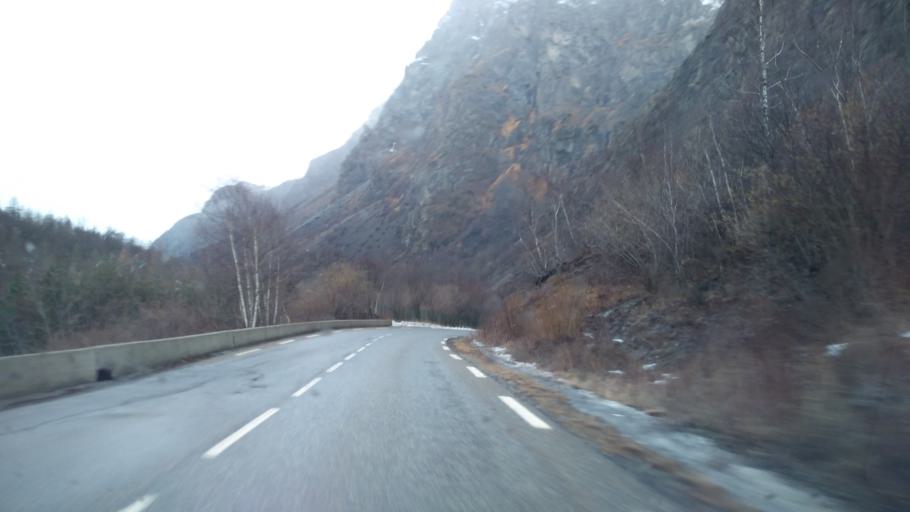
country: FR
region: Rhone-Alpes
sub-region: Departement de l'Isere
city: Mont-de-Lans
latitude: 45.0362
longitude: 6.2166
